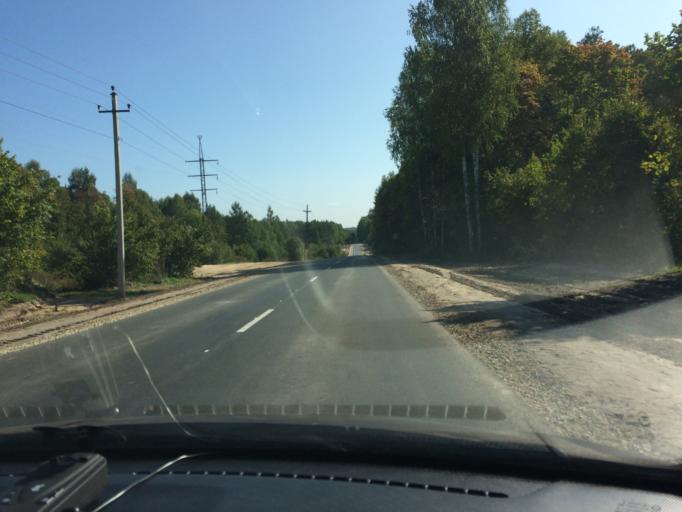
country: RU
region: Mariy-El
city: Sovetskiy
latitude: 56.5460
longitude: 48.4231
